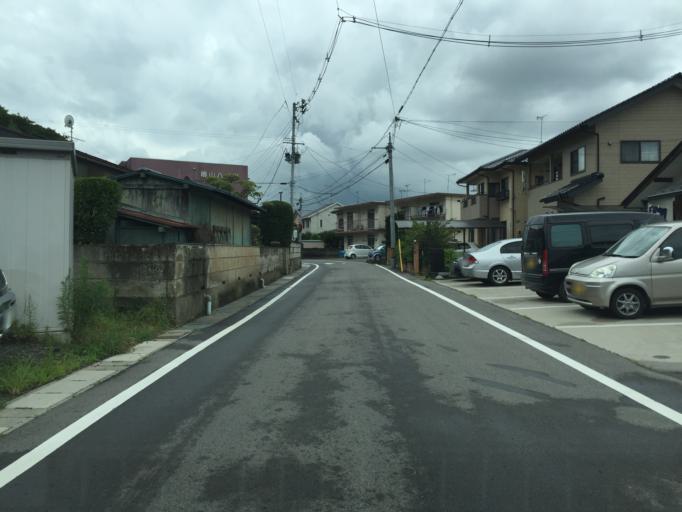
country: JP
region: Fukushima
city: Fukushima-shi
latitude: 37.7442
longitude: 140.4754
